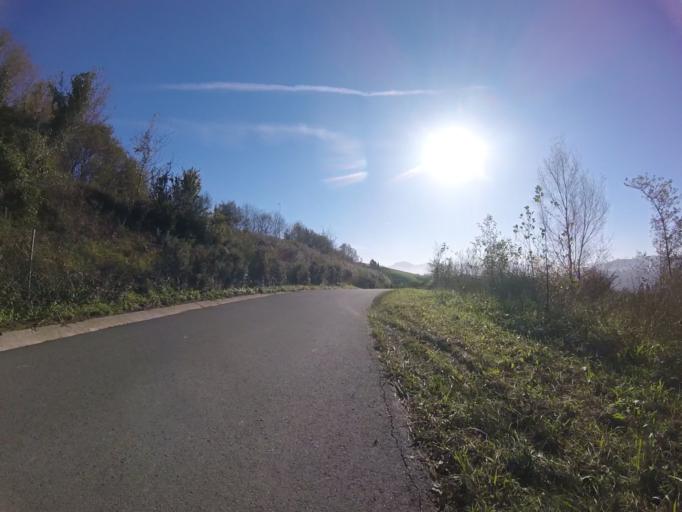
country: ES
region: Basque Country
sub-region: Provincia de Guipuzcoa
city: Usurbil
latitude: 43.2863
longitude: -2.0333
